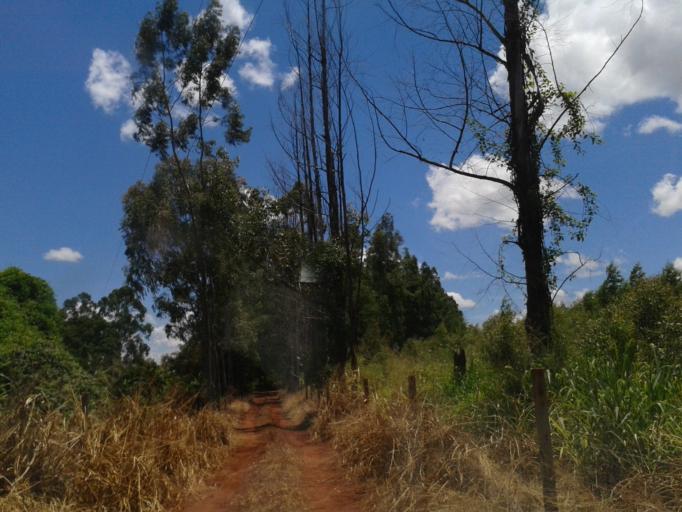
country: BR
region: Minas Gerais
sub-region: Centralina
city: Centralina
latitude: -18.7009
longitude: -49.1709
